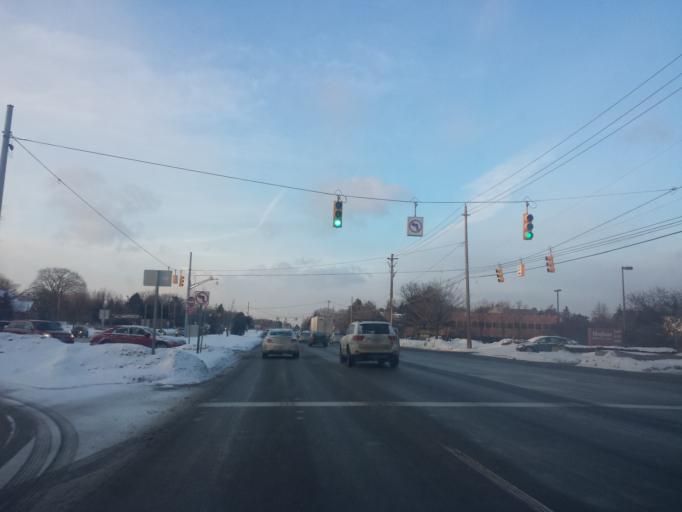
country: US
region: Michigan
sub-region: Oakland County
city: Bingham Farms
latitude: 42.5133
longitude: -83.2855
